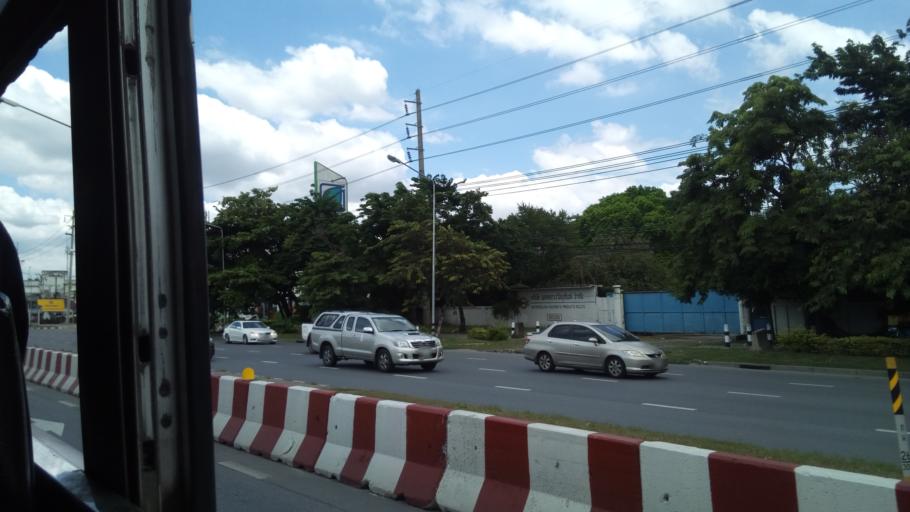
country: TH
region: Bangkok
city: Sai Mai
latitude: 13.9378
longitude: 100.6248
